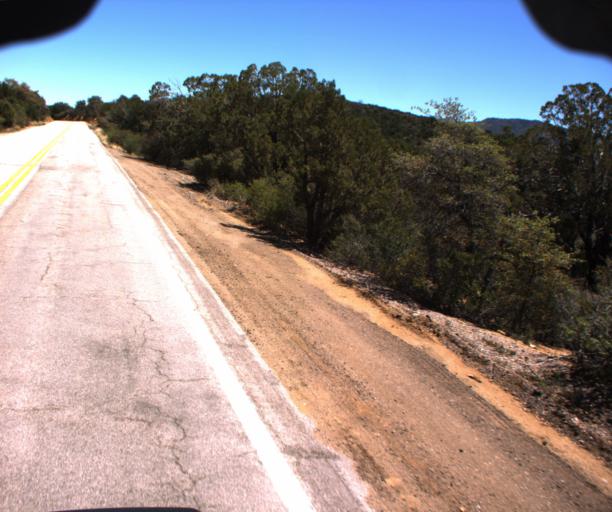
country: US
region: Arizona
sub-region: Yavapai County
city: Prescott
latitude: 34.4283
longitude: -112.5475
